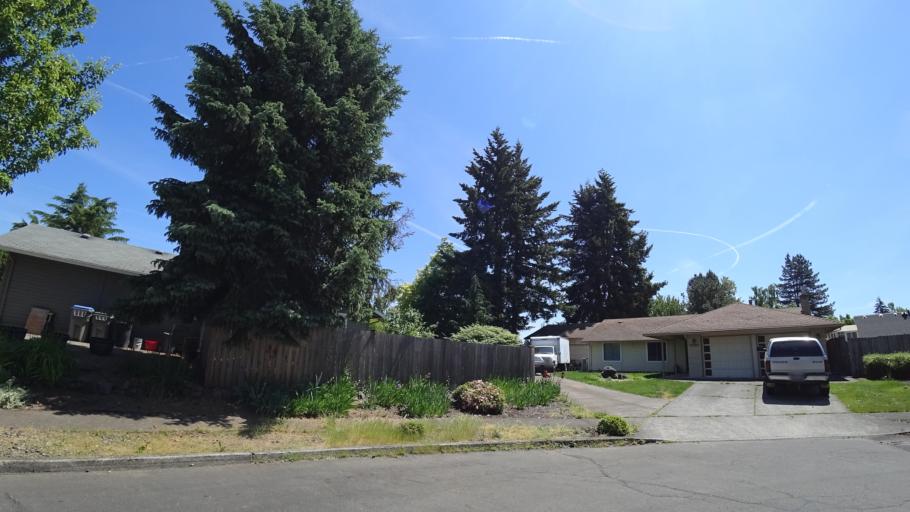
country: US
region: Oregon
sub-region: Washington County
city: King City
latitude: 45.4320
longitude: -122.8079
